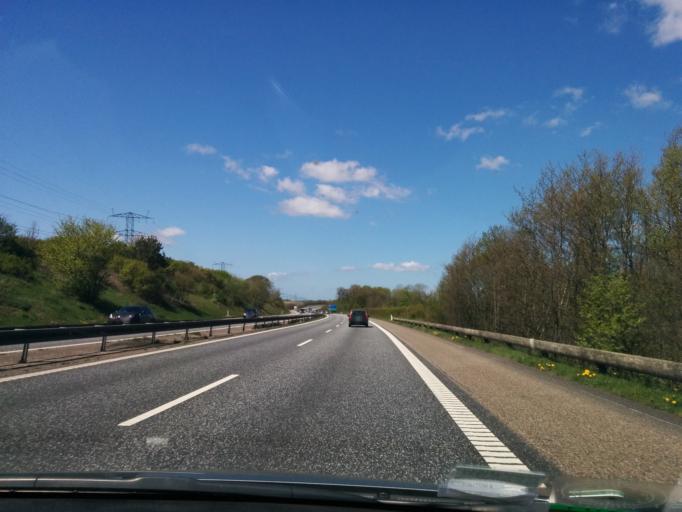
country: DK
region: Central Jutland
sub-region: Arhus Kommune
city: Trige
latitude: 56.2941
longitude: 10.1342
